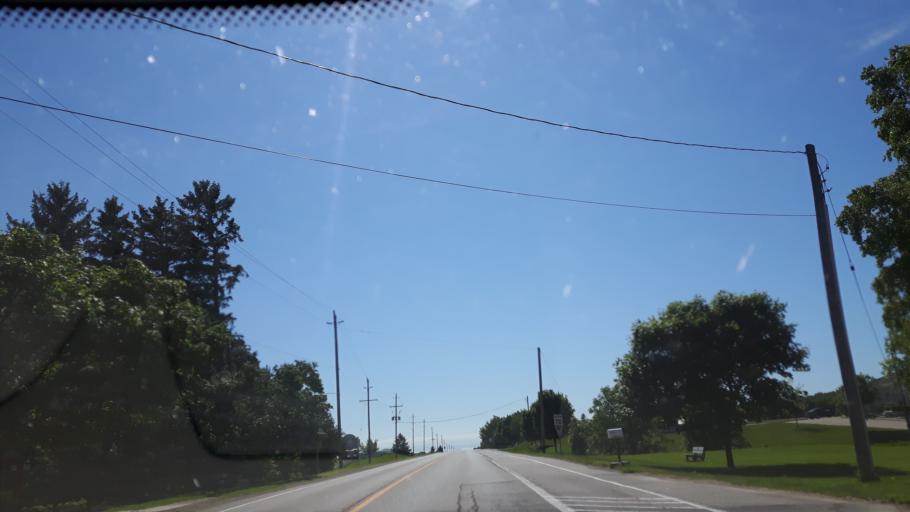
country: CA
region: Ontario
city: Bluewater
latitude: 43.4205
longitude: -81.6311
